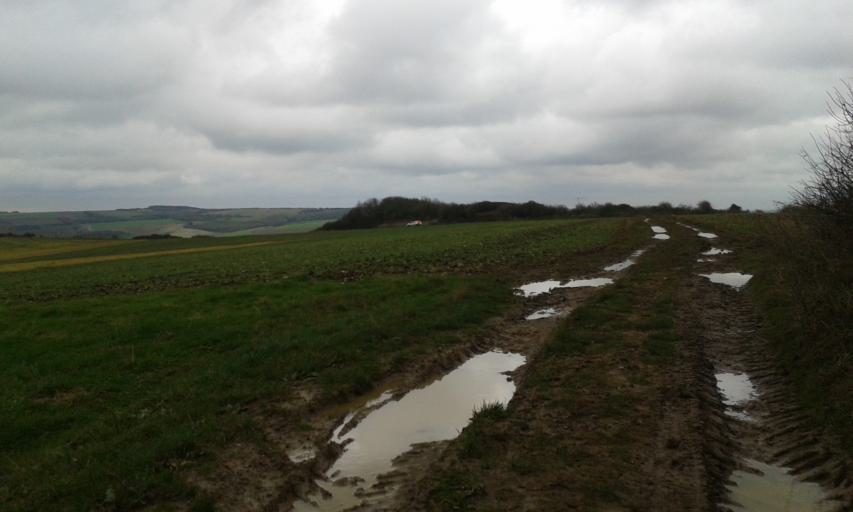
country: FR
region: Nord-Pas-de-Calais
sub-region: Departement du Pas-de-Calais
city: Wissant
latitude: 50.8953
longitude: 1.7115
